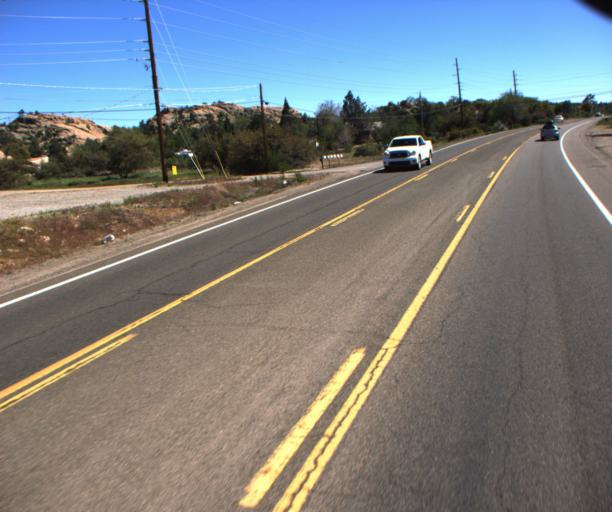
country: US
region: Arizona
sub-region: Yavapai County
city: Prescott
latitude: 34.5999
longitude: -112.4247
